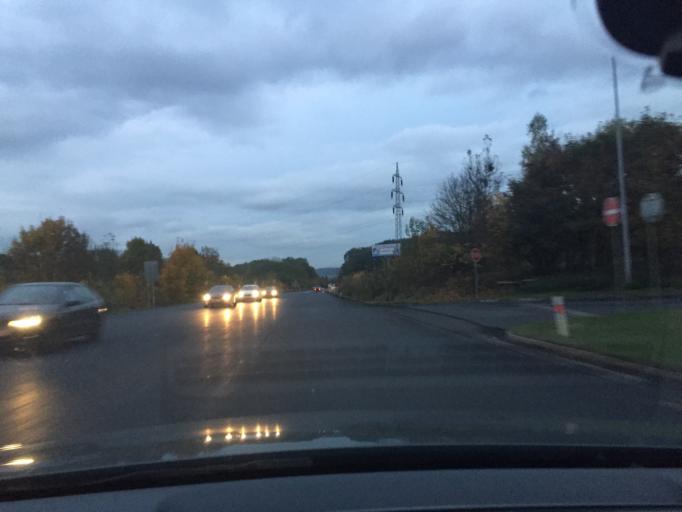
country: CZ
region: Ustecky
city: Bystrany
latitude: 50.6305
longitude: 13.8436
